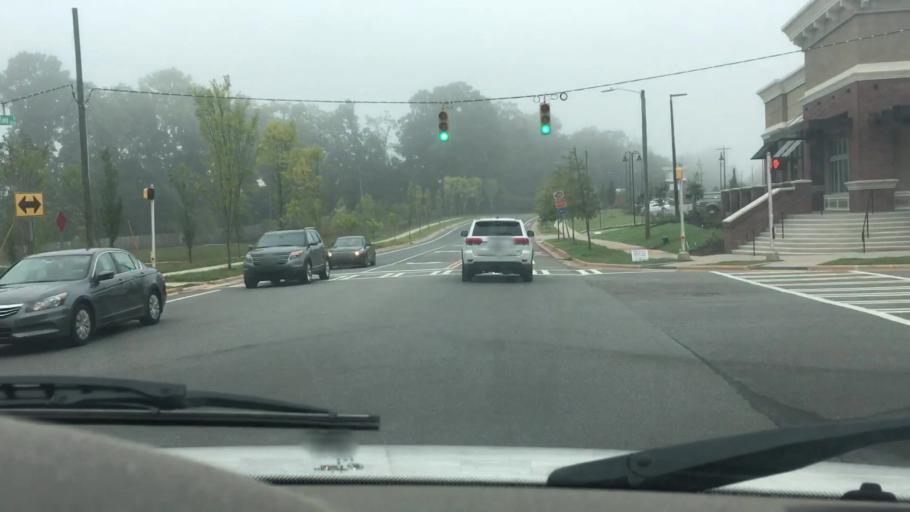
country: US
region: North Carolina
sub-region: Mecklenburg County
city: Huntersville
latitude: 35.3726
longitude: -80.7895
